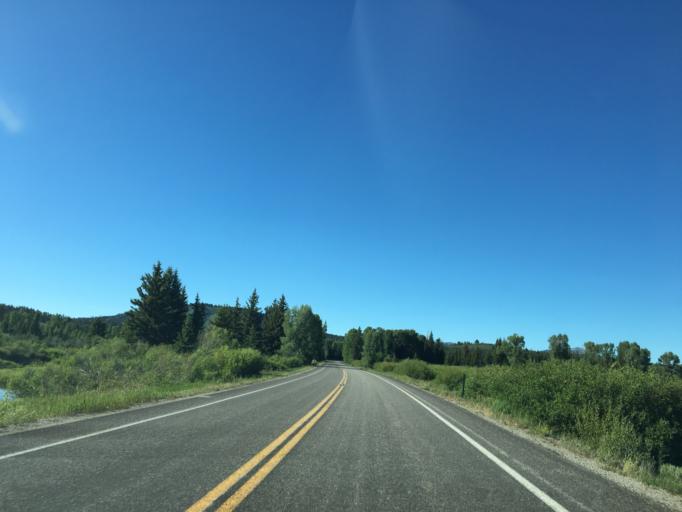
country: US
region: Wyoming
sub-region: Teton County
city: Jackson
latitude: 43.8317
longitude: -110.5133
